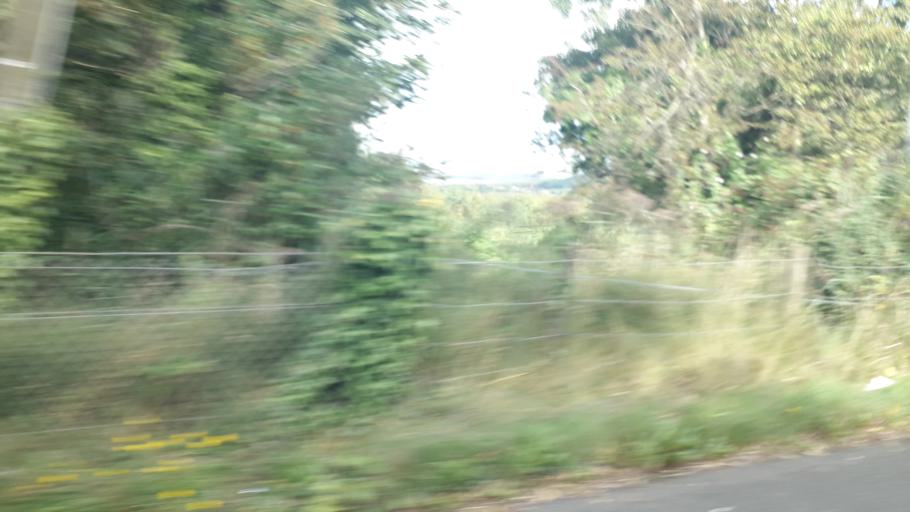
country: IE
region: Leinster
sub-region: Lu
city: Blackrock
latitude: 54.0166
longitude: -6.3243
